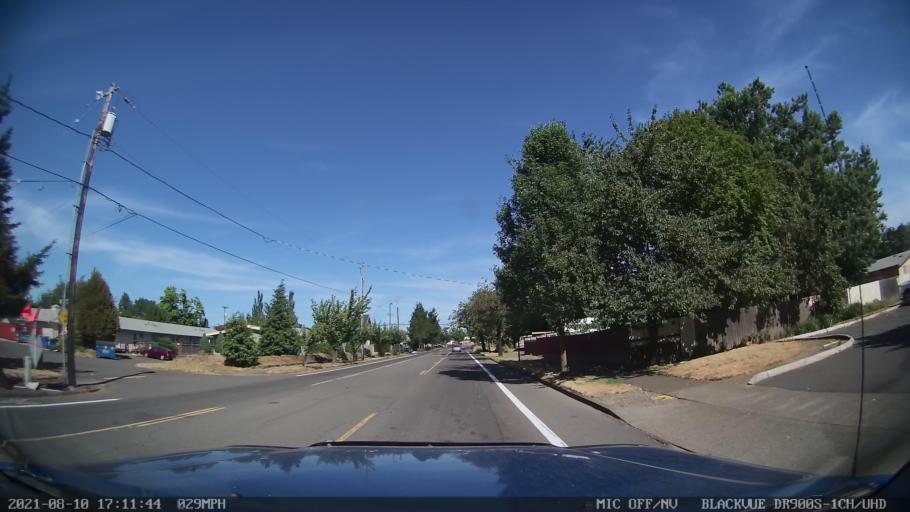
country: US
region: Oregon
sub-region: Marion County
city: Salem
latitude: 44.9619
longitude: -123.0180
